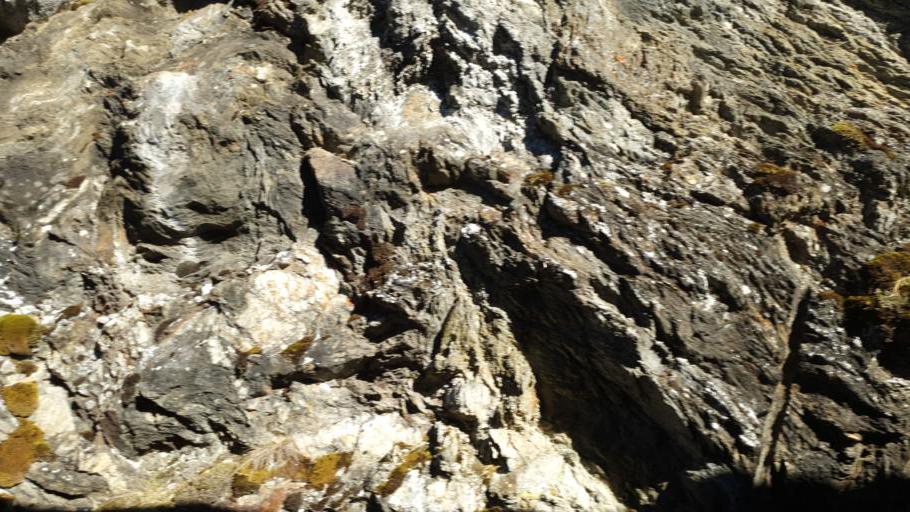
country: NO
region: Sor-Trondelag
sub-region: Meldal
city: Meldal
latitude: 63.1717
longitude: 9.7488
